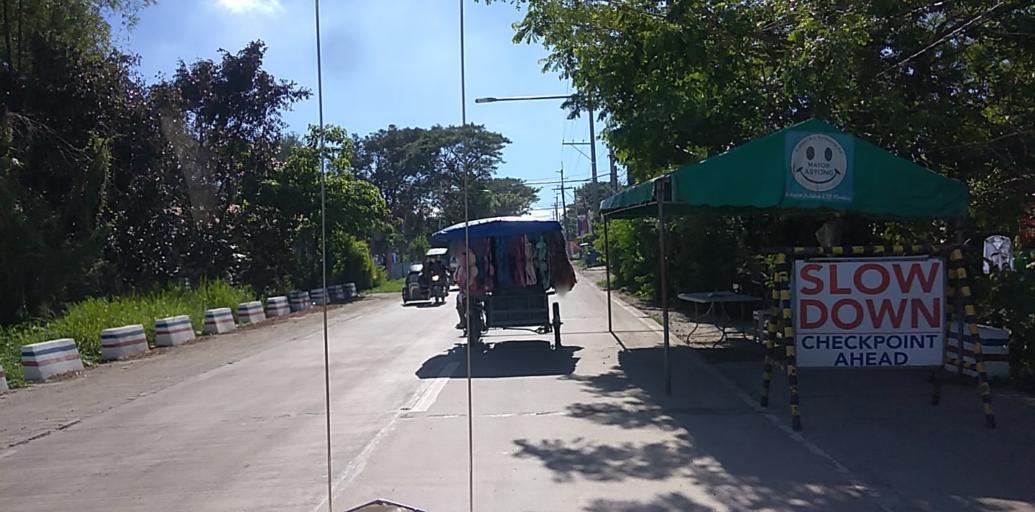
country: PH
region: Central Luzon
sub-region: Province of Pampanga
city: San Luis
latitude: 15.0543
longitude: 120.7788
